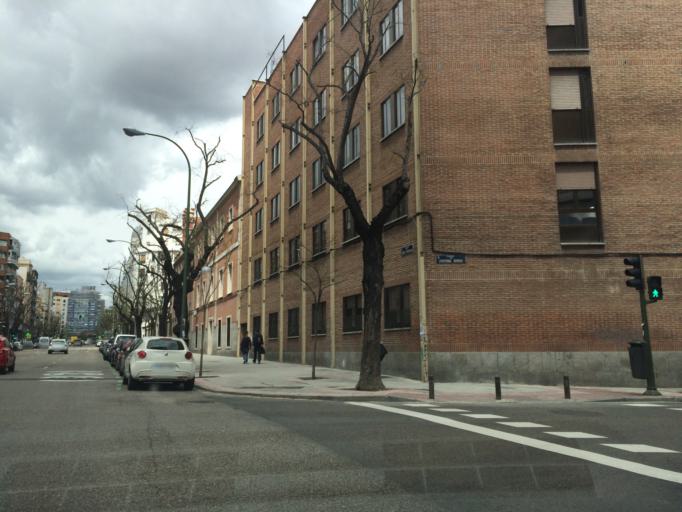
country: ES
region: Madrid
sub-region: Provincia de Madrid
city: Chamberi
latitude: 40.4431
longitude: -3.7022
